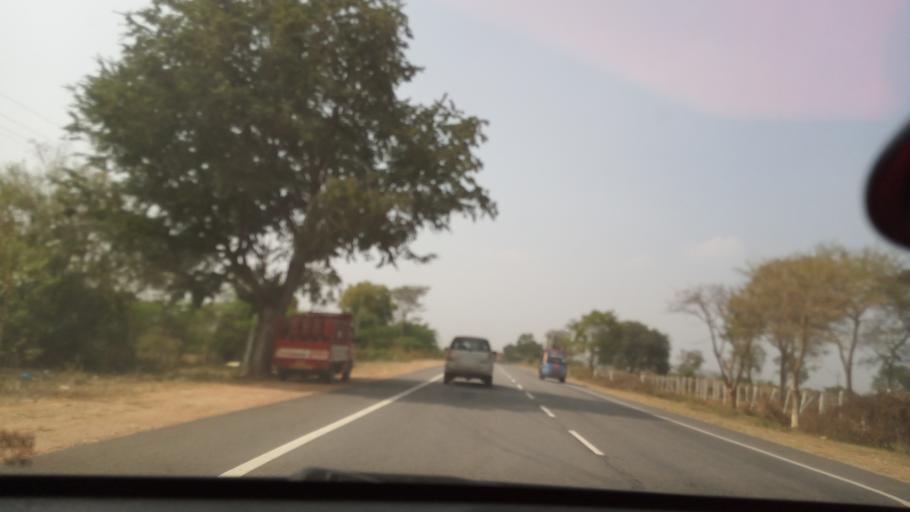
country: IN
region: Karnataka
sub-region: Mysore
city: Nanjangud
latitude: 12.0725
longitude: 76.7432
